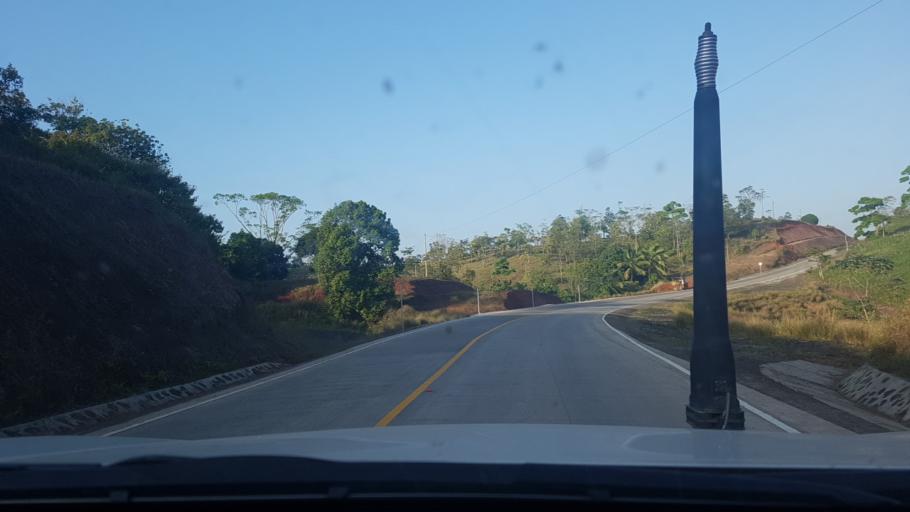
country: NI
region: Atlantico Sur
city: Rama
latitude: 11.8167
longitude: -84.0979
